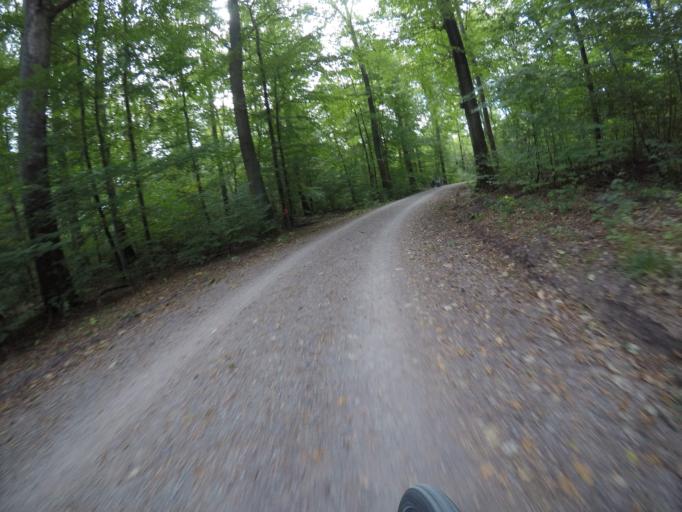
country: DE
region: Baden-Wuerttemberg
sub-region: Regierungsbezirk Stuttgart
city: Schonaich
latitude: 48.6720
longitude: 9.0507
